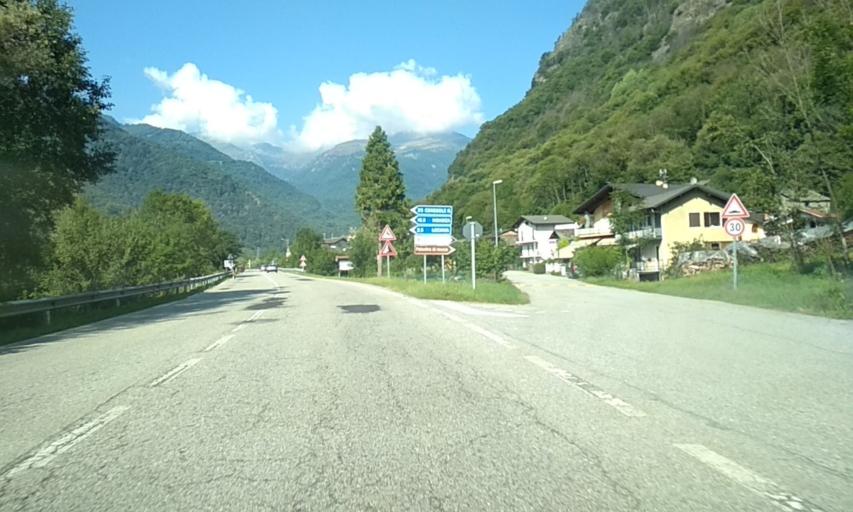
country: IT
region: Piedmont
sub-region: Provincia di Torino
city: Ribordone
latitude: 45.4071
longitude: 7.5074
